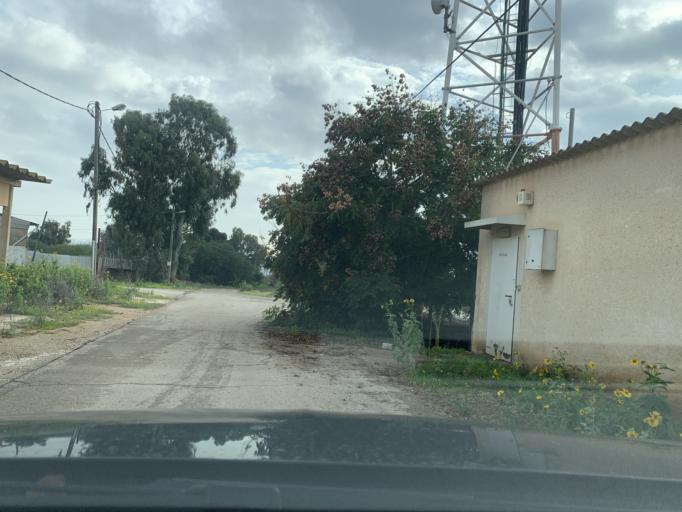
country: PS
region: West Bank
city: Qalqilyah
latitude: 32.1950
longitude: 34.9507
